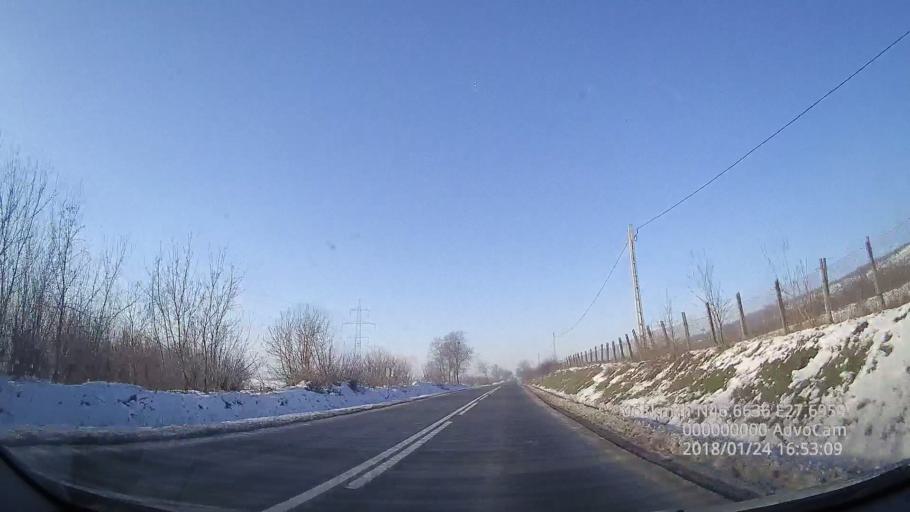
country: RO
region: Vaslui
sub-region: Municipiul Vaslui
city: Brodoc
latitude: 46.6638
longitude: 27.6956
